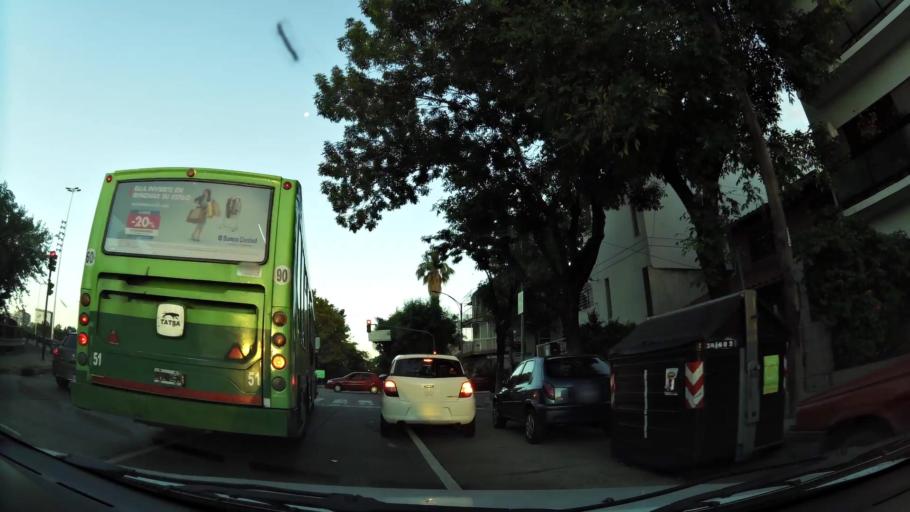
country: AR
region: Buenos Aires
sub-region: Partido de Vicente Lopez
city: Olivos
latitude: -34.5418
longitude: -58.4806
